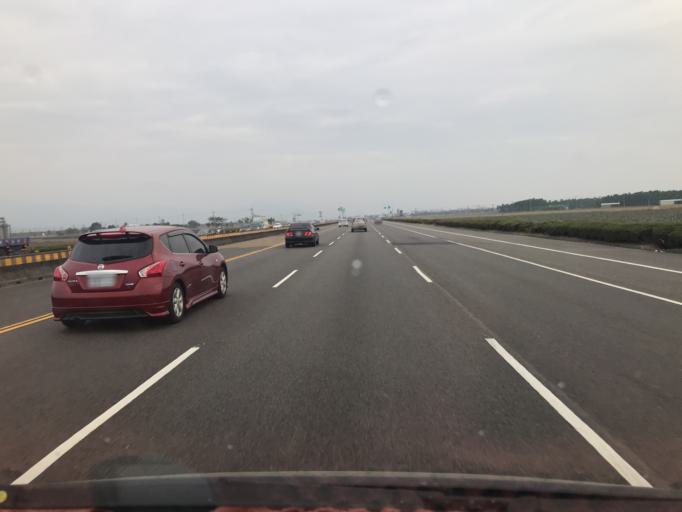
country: TW
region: Taiwan
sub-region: Pingtung
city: Pingtung
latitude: 22.4334
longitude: 120.5713
